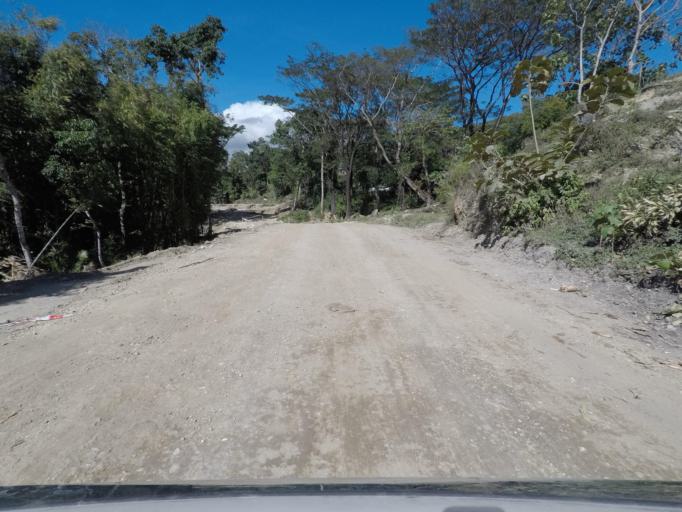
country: TL
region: Baucau
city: Venilale
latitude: -8.6494
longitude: 126.3720
